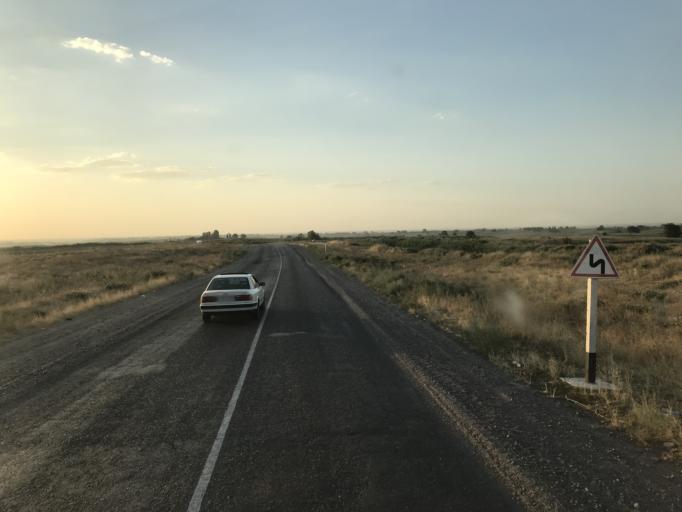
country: UZ
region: Toshkent
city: Yangiyul
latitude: 41.3404
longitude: 68.8786
